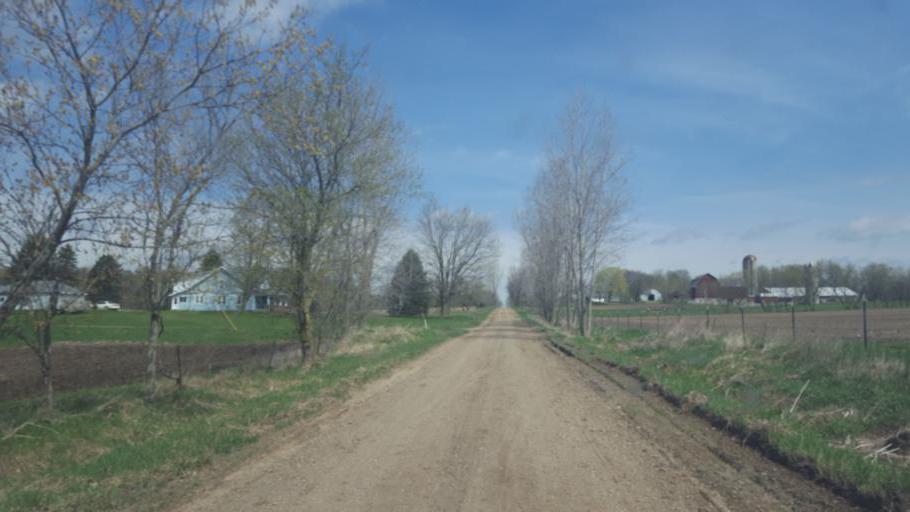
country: US
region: Michigan
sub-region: Montcalm County
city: Edmore
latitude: 43.4867
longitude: -84.9460
